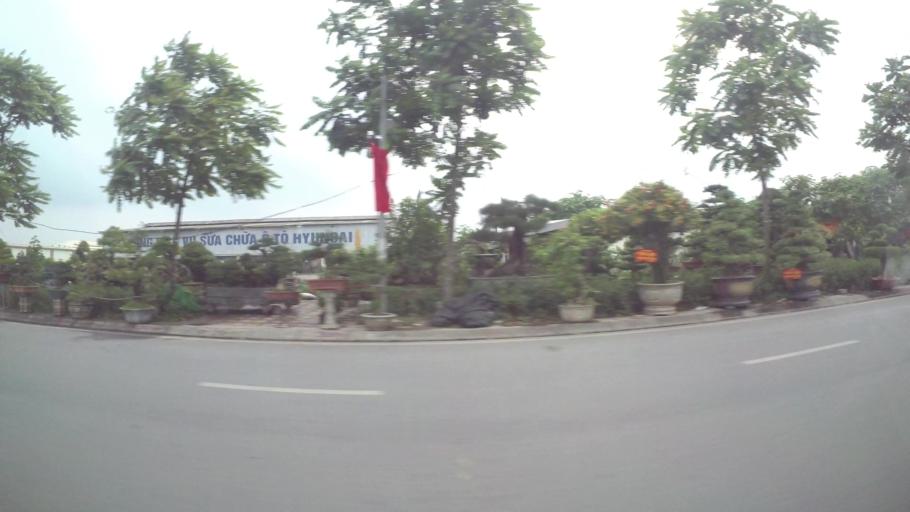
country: VN
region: Ha Noi
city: Hoan Kiem
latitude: 21.0538
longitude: 105.8929
